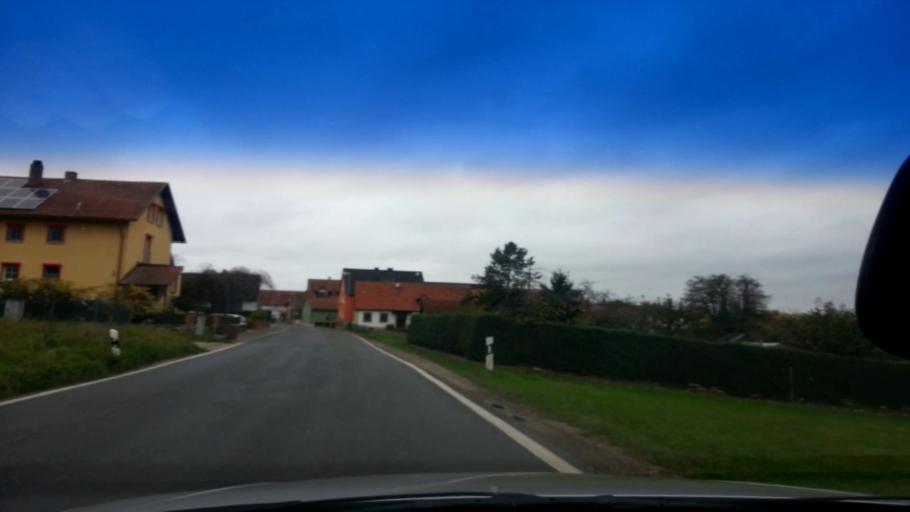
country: DE
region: Bavaria
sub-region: Upper Franconia
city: Burgebrach
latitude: 49.8249
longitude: 10.7798
